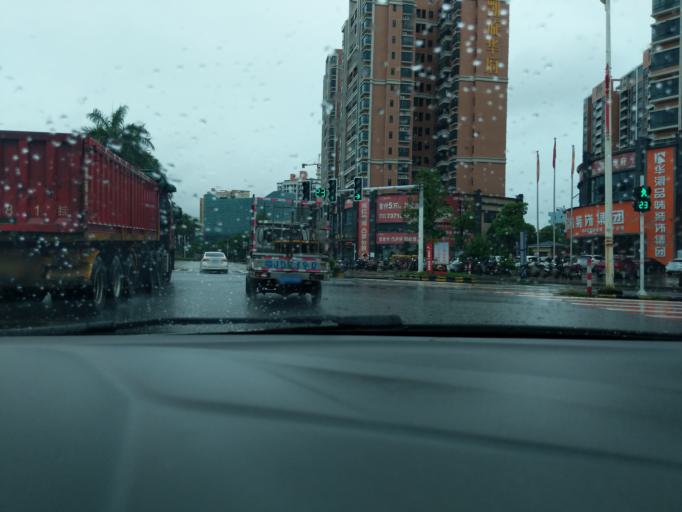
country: CN
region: Guangdong
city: Pingshi
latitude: 22.2024
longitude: 112.3288
